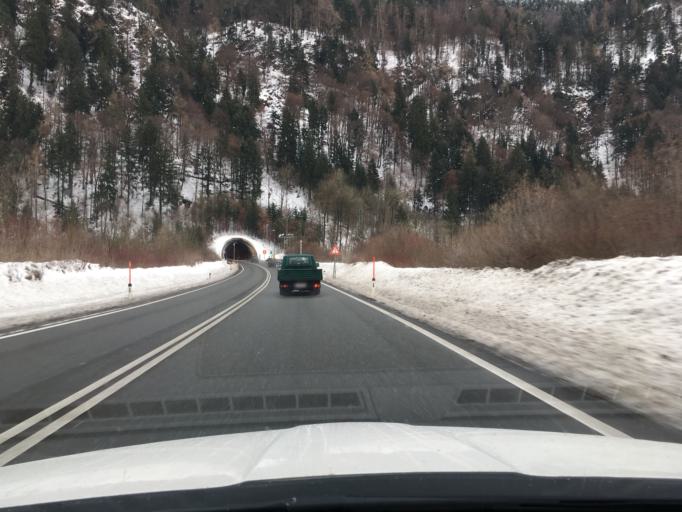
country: AT
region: Tyrol
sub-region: Politischer Bezirk Schwaz
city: Strass im Zillertal
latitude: 47.3946
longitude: 11.8104
